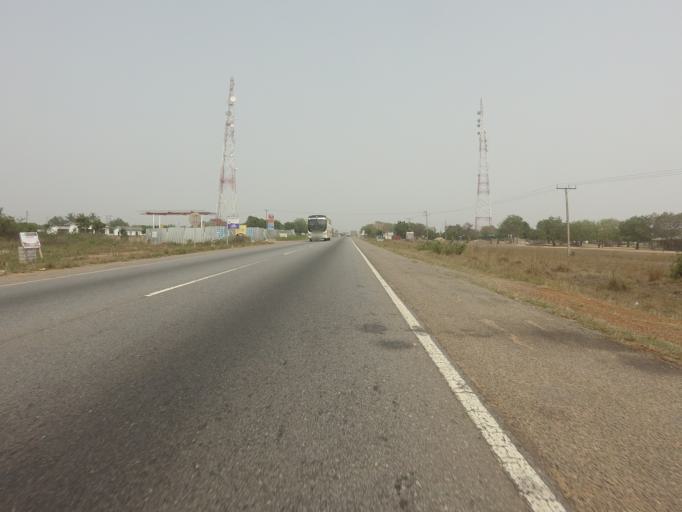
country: GH
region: Greater Accra
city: Tema
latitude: 5.8647
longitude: 0.2870
